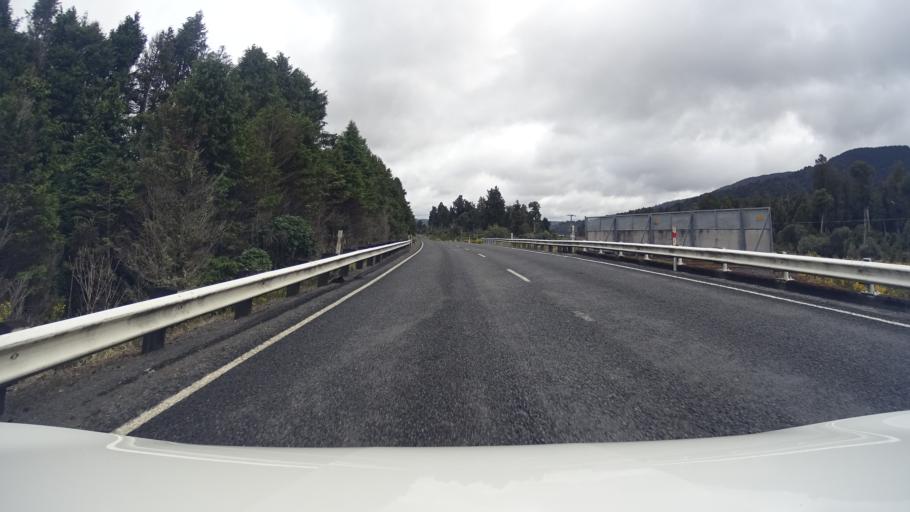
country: NZ
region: Manawatu-Wanganui
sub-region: Ruapehu District
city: Waiouru
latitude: -39.2426
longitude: 175.3916
